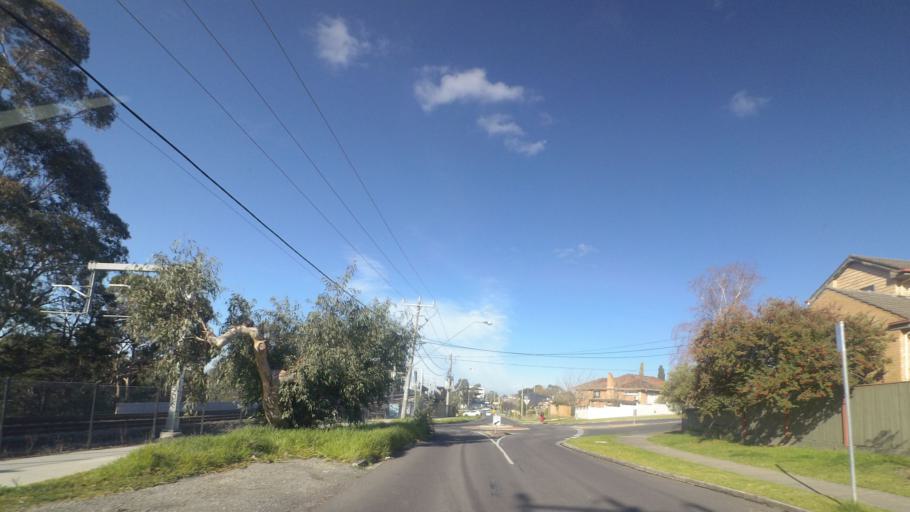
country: AU
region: Victoria
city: Macleod
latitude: -37.7405
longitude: 145.0654
